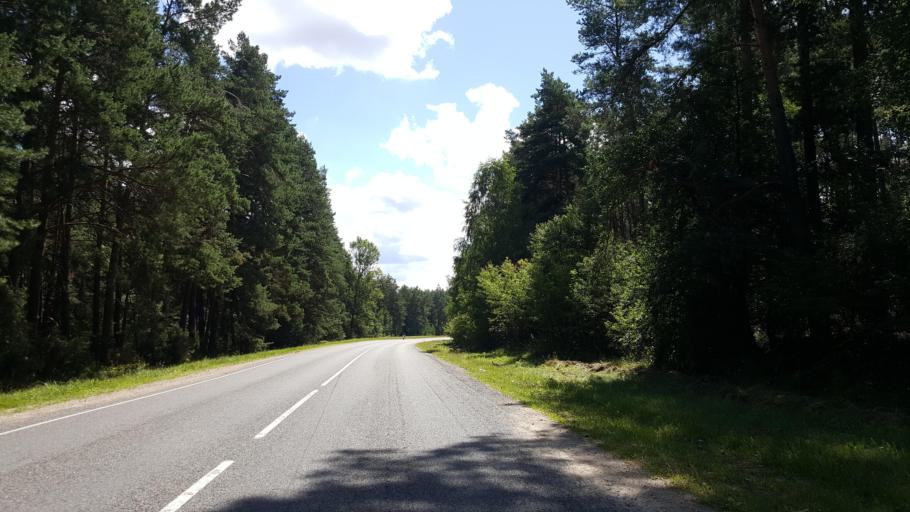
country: BY
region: Brest
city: Kamyanyets
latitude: 52.3853
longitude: 23.8546
